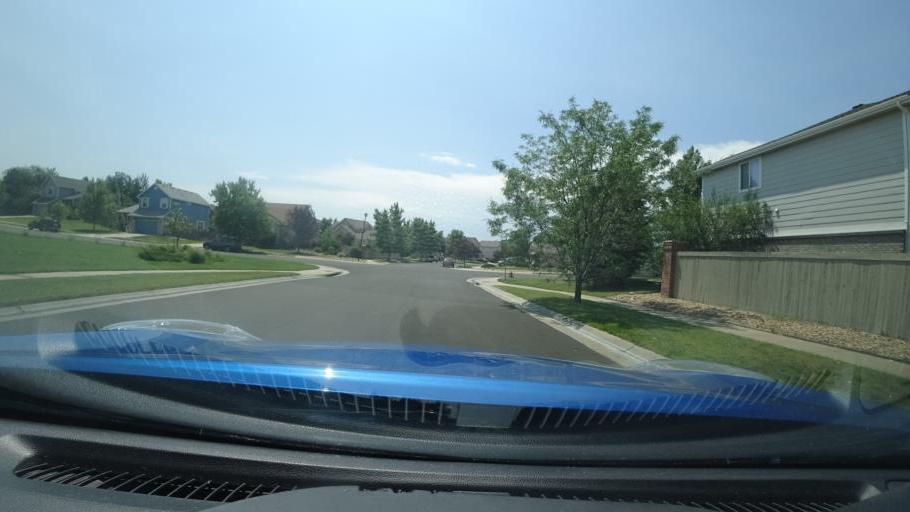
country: US
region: Colorado
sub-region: Adams County
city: Aurora
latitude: 39.6730
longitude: -104.7614
